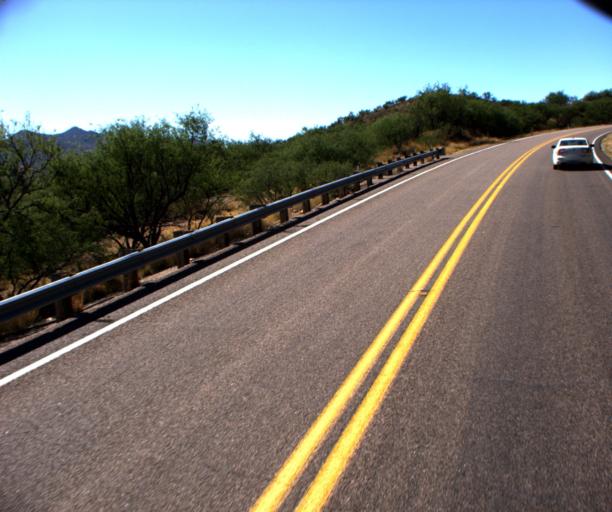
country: US
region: Arizona
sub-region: Santa Cruz County
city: Rio Rico
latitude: 31.4956
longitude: -110.8112
